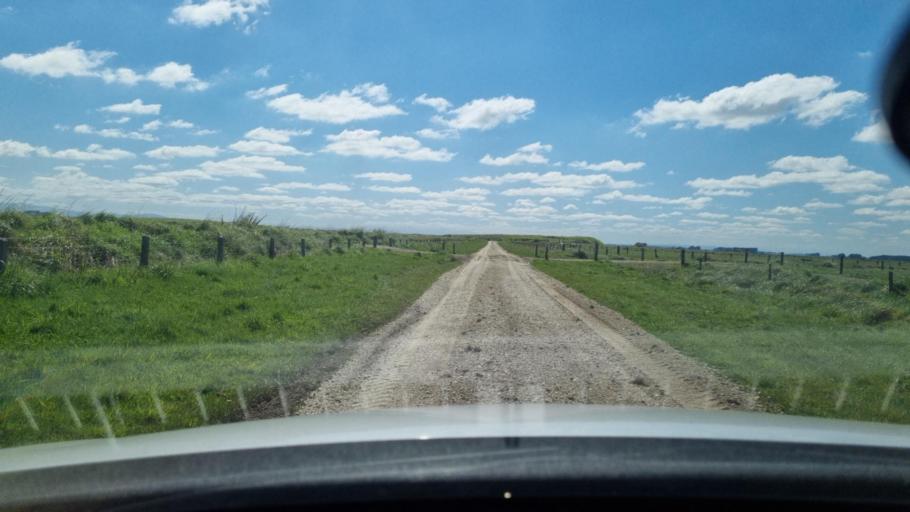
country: NZ
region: Southland
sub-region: Invercargill City
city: Invercargill
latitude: -46.3883
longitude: 168.2588
